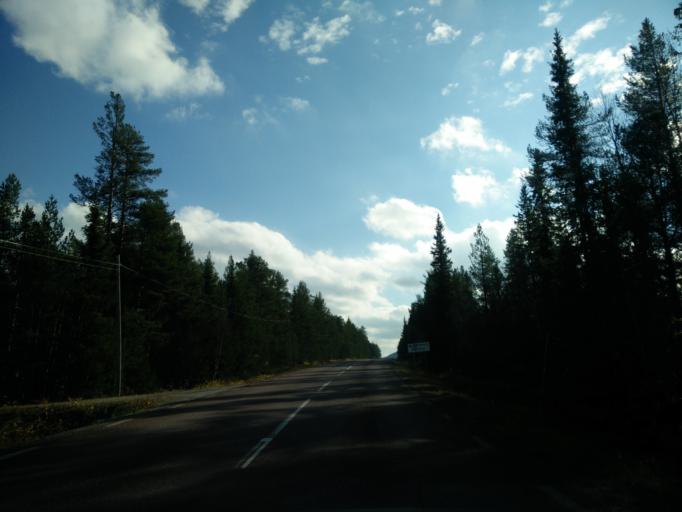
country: NO
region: Hedmark
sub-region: Engerdal
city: Engerdal
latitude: 62.5021
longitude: 12.6250
